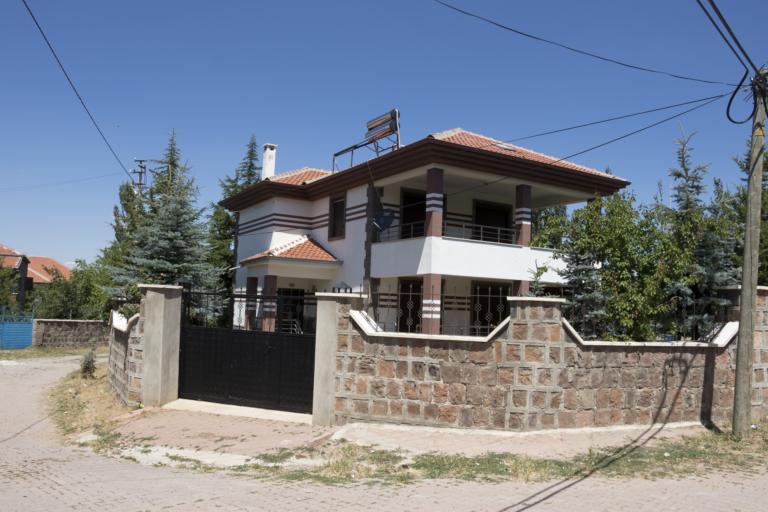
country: TR
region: Kayseri
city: Toklar
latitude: 38.4065
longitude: 36.0820
